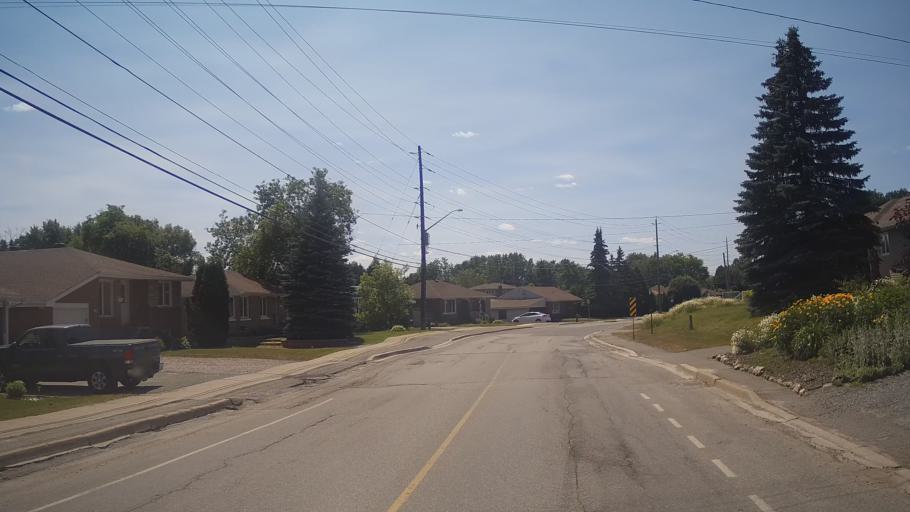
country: CA
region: Ontario
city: Greater Sudbury
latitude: 46.4597
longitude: -81.0206
